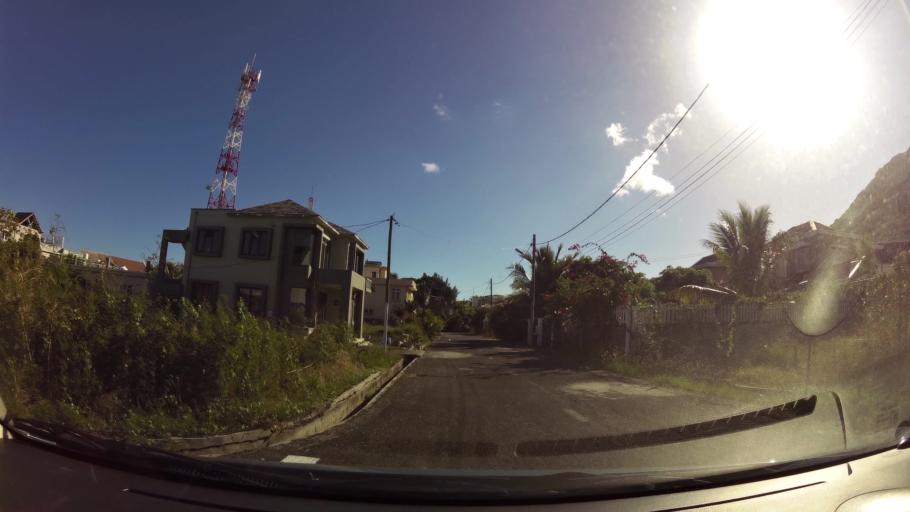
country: MU
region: Black River
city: Grande Riviere Noire
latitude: -20.3518
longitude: 57.3641
